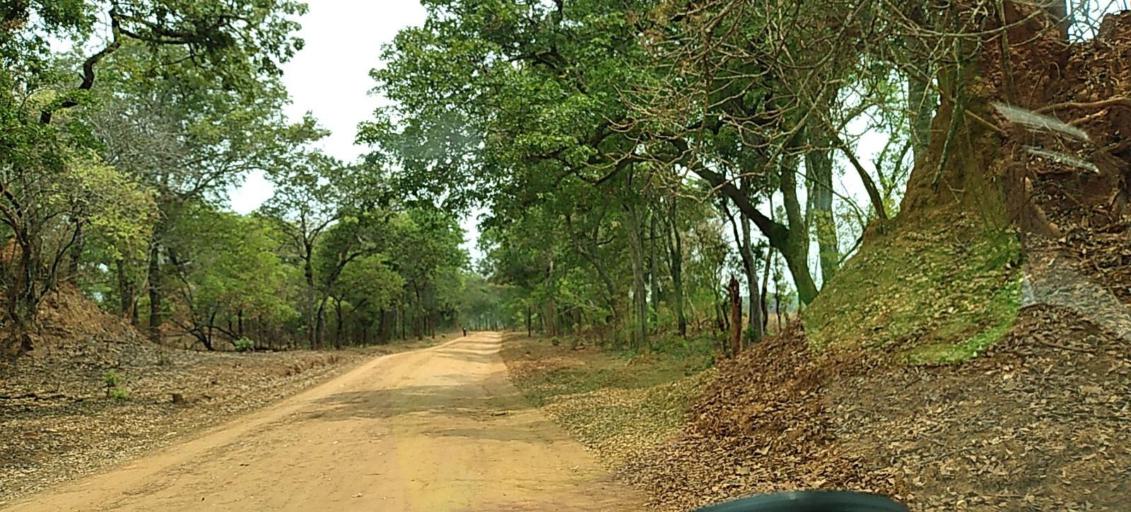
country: ZM
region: North-Western
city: Solwezi
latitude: -12.8139
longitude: 26.5365
